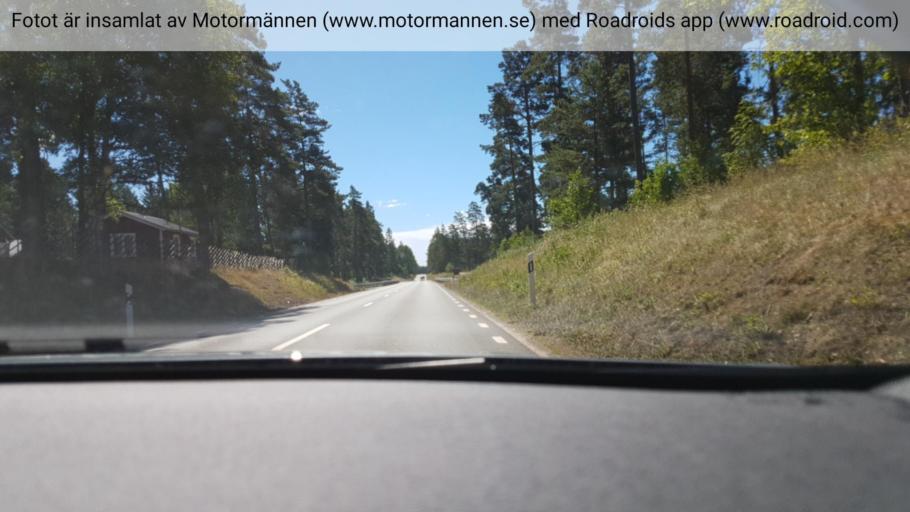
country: SE
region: Joenkoeping
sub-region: Mullsjo Kommun
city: Mullsjoe
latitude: 57.8920
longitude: 13.8438
